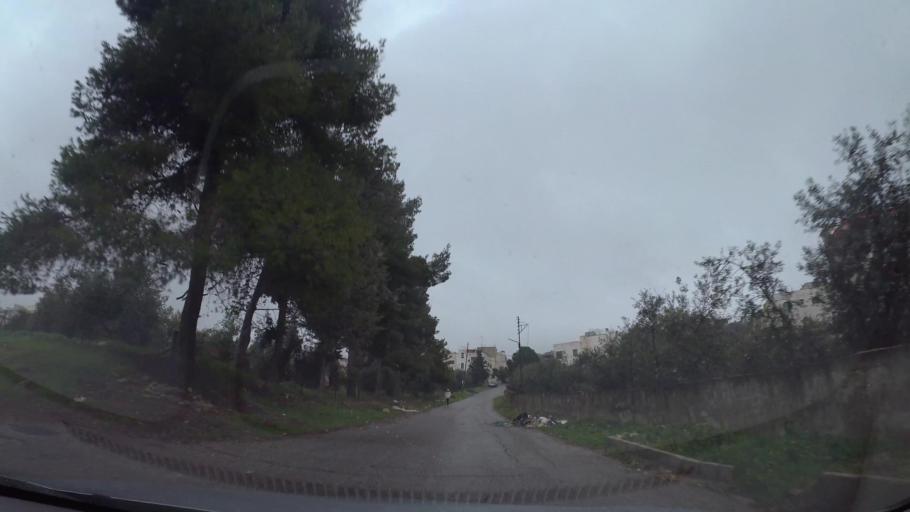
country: JO
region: Amman
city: Al Jubayhah
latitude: 32.0356
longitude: 35.8351
